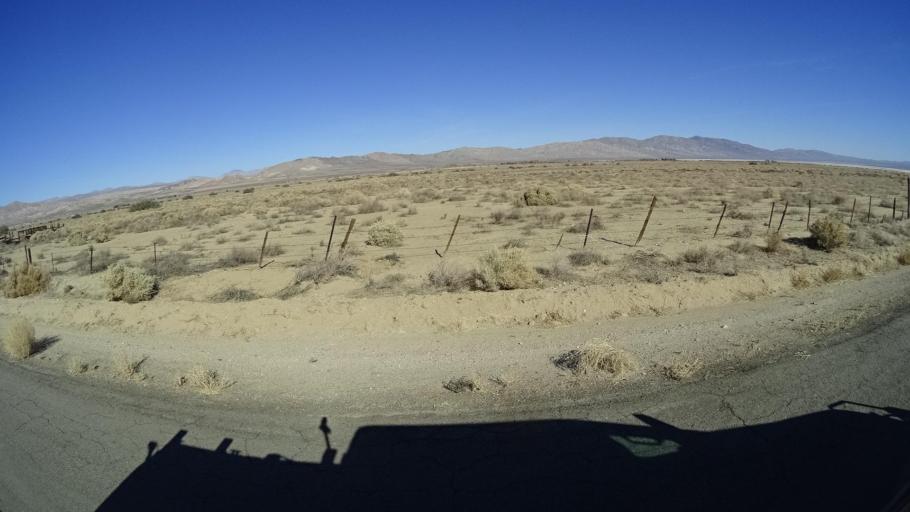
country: US
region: California
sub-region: Kern County
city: California City
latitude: 35.2869
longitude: -117.9322
